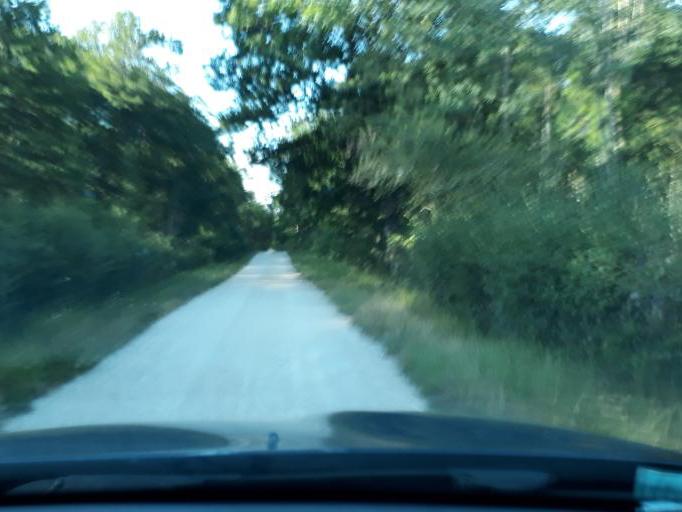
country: FR
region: Centre
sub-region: Departement du Loiret
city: Chaingy
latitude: 47.8996
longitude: 1.7408
